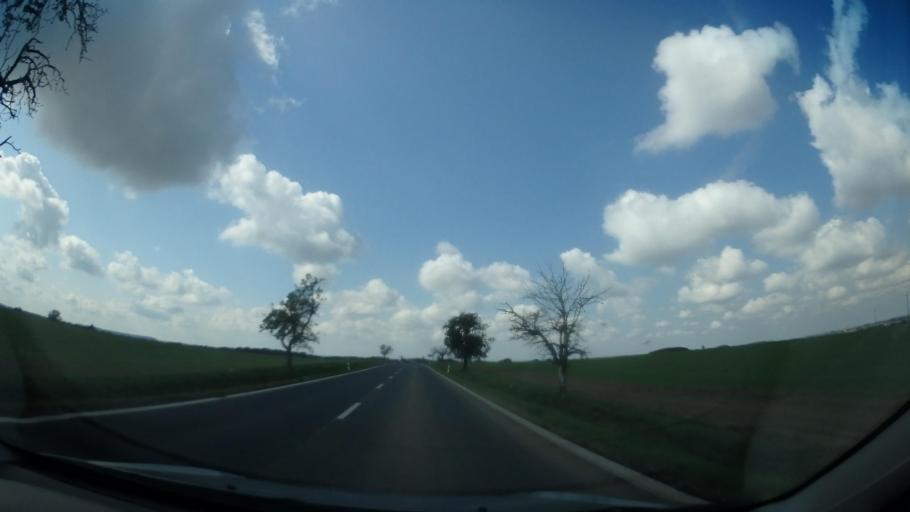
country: CZ
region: Central Bohemia
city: Suchdol
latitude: 49.9529
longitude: 15.1551
